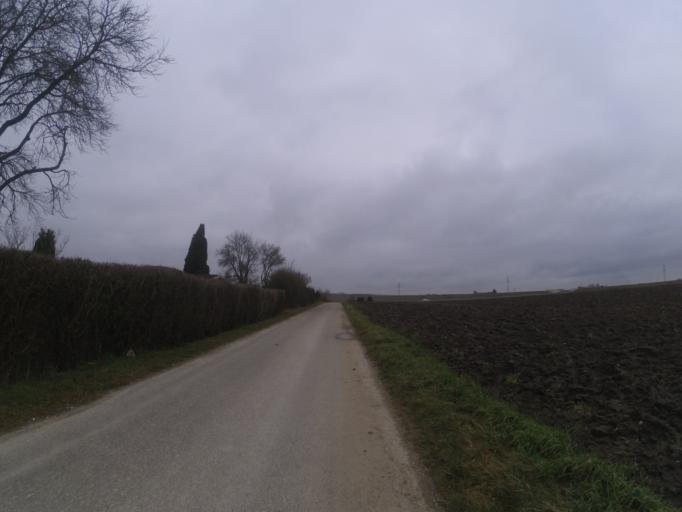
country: DE
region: Baden-Wuerttemberg
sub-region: Tuebingen Region
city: Dornstadt
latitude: 48.4639
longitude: 9.9340
